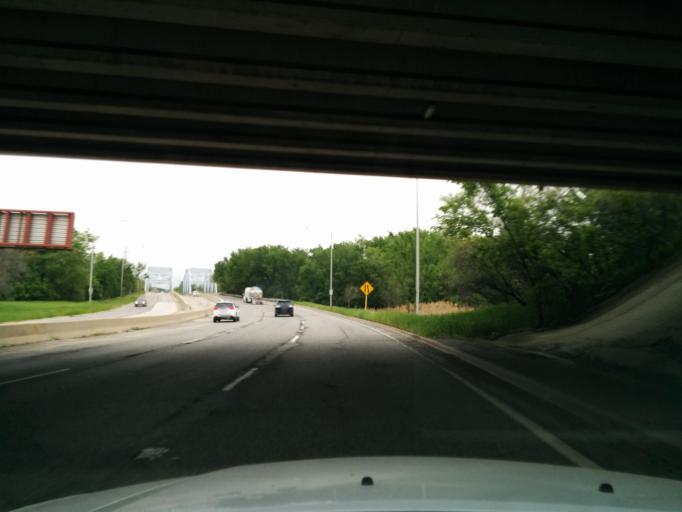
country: US
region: Illinois
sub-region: Cook County
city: Palos Park
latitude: 41.6829
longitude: -87.8555
